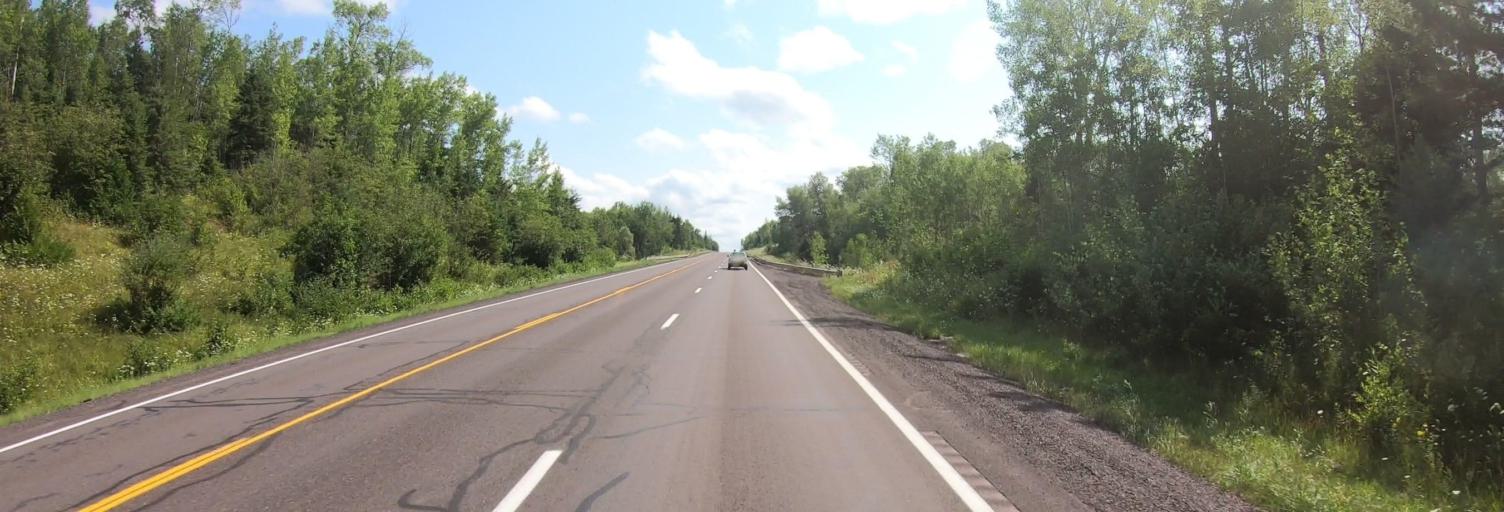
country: US
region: Michigan
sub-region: Ontonagon County
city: Ontonagon
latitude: 46.6785
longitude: -89.1667
